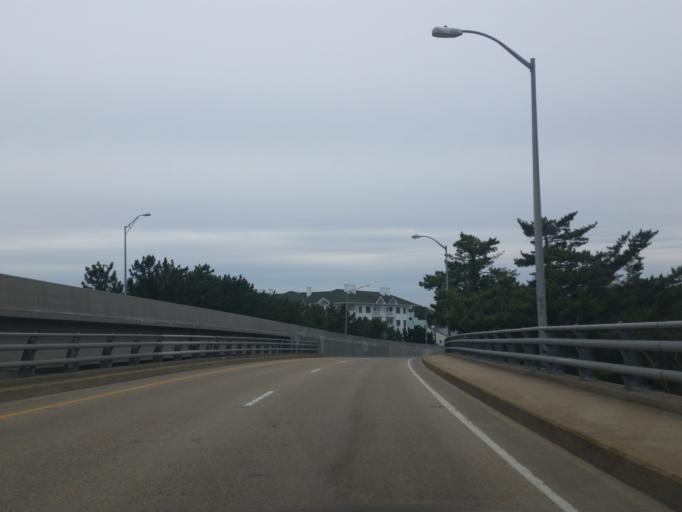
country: US
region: Virginia
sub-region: City of Virginia Beach
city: Virginia Beach
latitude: 36.8311
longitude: -75.9724
